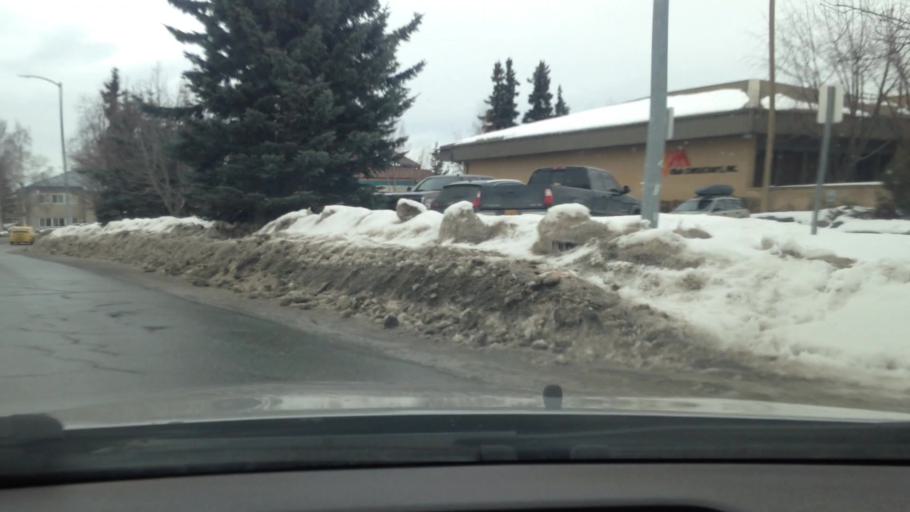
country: US
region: Alaska
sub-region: Anchorage Municipality
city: Anchorage
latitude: 61.1376
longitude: -149.8475
